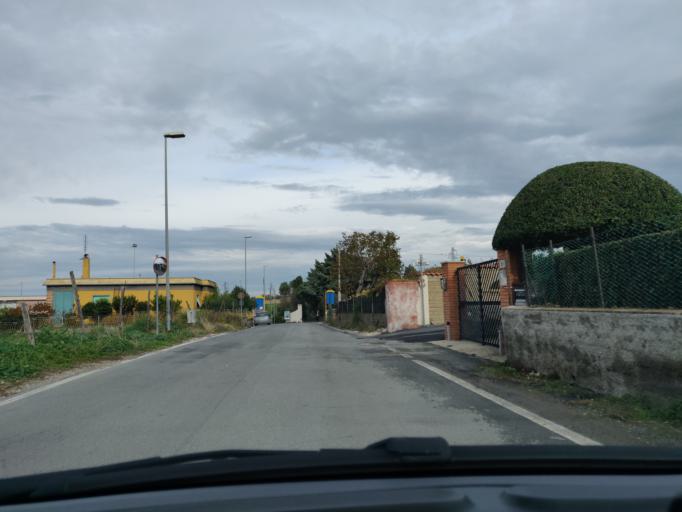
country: IT
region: Latium
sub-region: Citta metropolitana di Roma Capitale
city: Civitavecchia
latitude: 42.1035
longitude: 11.8122
